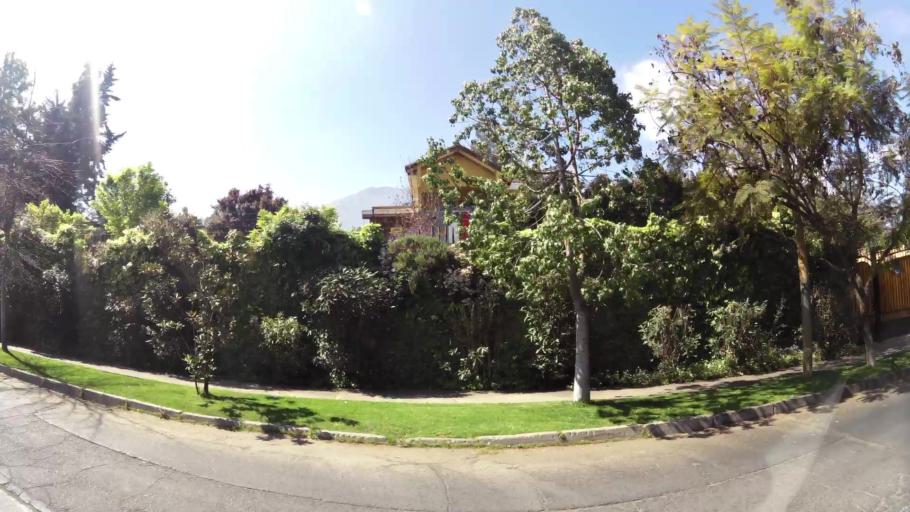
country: CL
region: Santiago Metropolitan
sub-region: Provincia de Santiago
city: Villa Presidente Frei, Nunoa, Santiago, Chile
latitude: -33.4522
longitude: -70.5249
